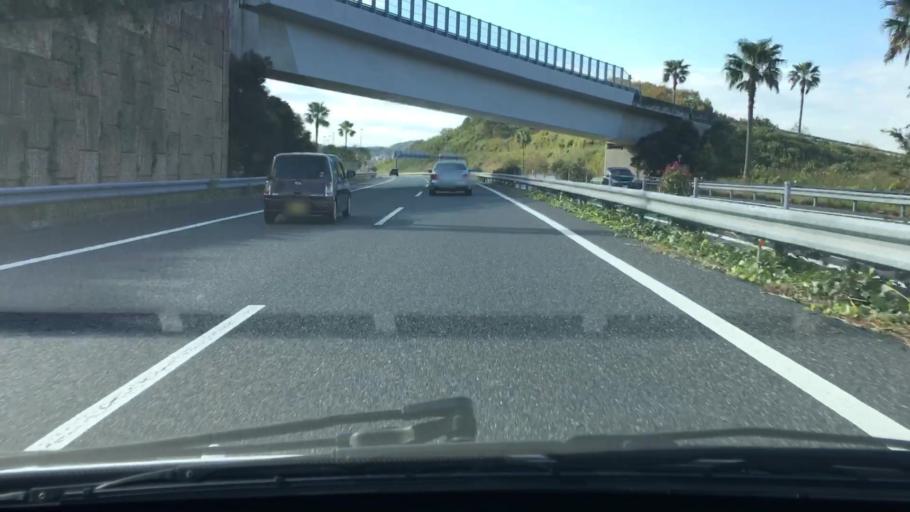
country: JP
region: Chiba
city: Kisarazu
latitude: 35.3544
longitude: 139.9489
